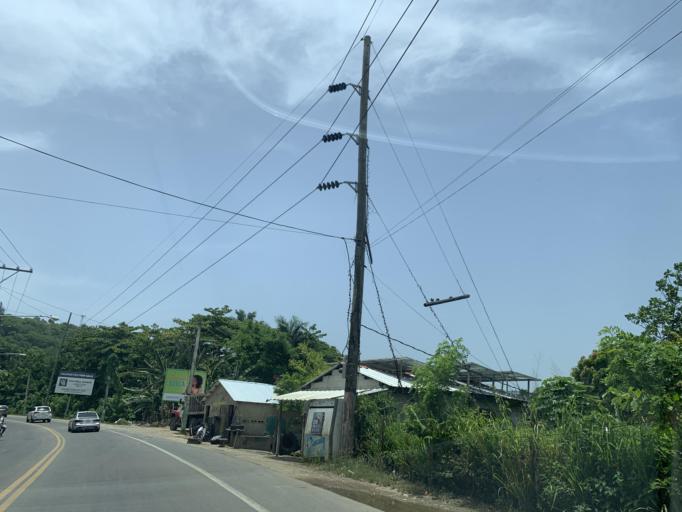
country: DO
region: Puerto Plata
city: Cabarete
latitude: 19.7450
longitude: -70.5211
